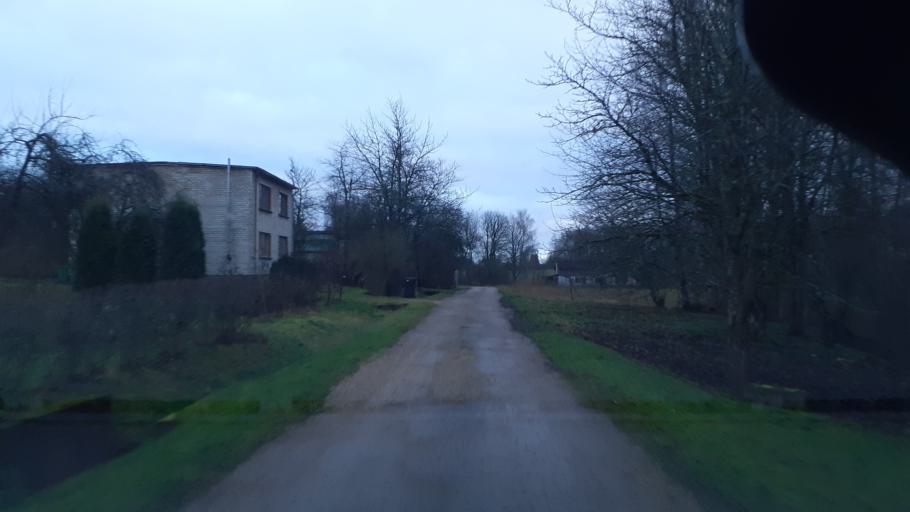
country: LV
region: Alsunga
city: Alsunga
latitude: 56.9034
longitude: 21.7002
